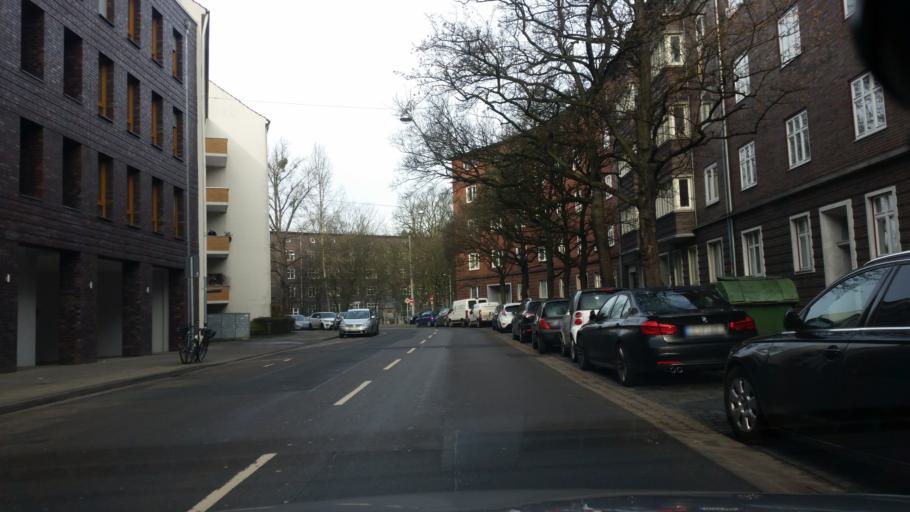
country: DE
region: Lower Saxony
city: Hannover
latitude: 52.3916
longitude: 9.7549
